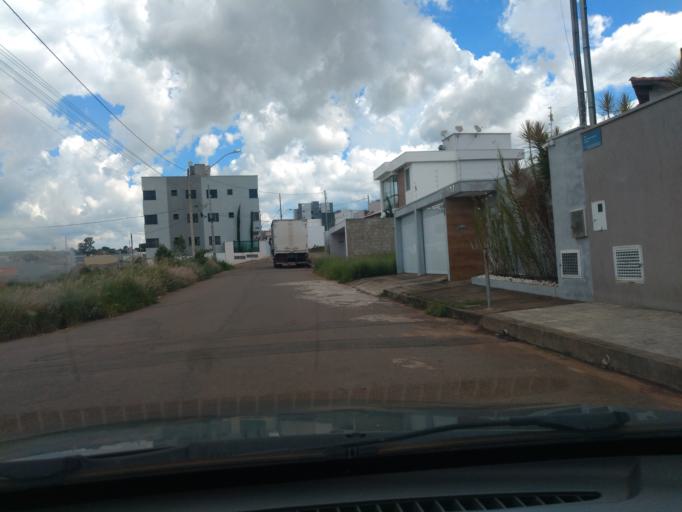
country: BR
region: Minas Gerais
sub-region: Tres Coracoes
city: Tres Coracoes
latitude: -21.6810
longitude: -45.2646
